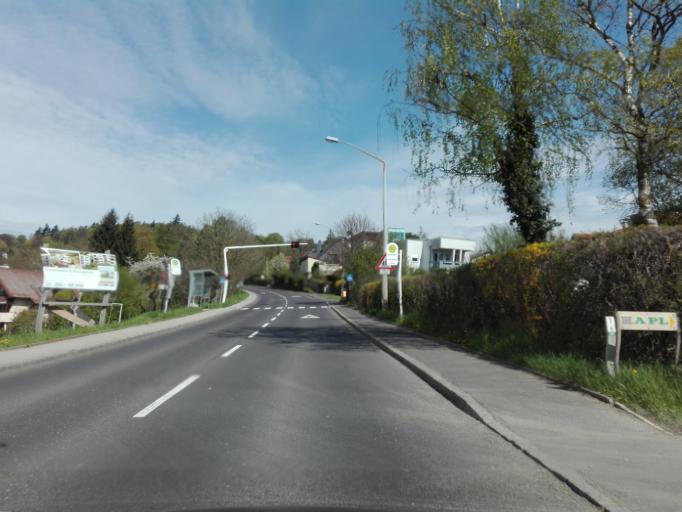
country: AT
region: Upper Austria
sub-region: Linz Stadt
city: Linz
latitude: 48.3134
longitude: 14.2603
